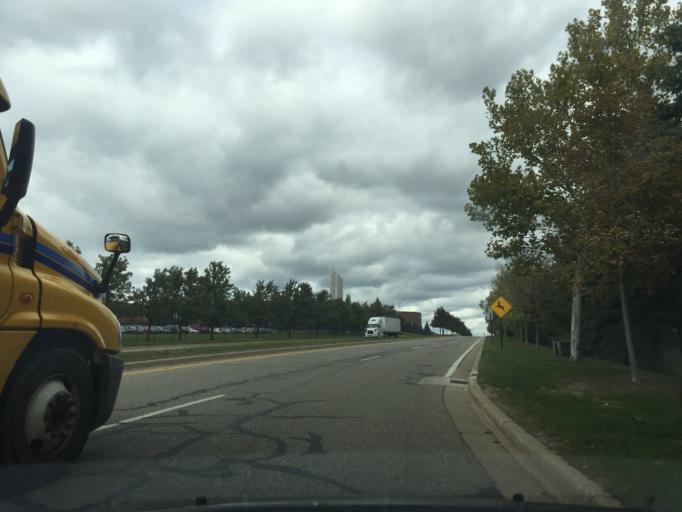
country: US
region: Michigan
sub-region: Oakland County
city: Auburn Hills
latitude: 42.6518
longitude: -83.2242
